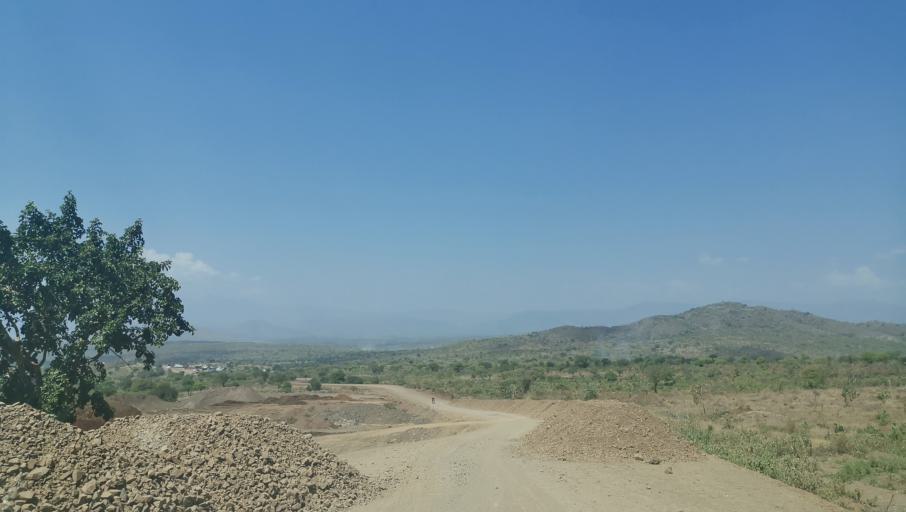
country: ET
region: Southern Nations, Nationalities, and People's Region
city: Arba Minch'
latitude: 6.3355
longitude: 37.3280
